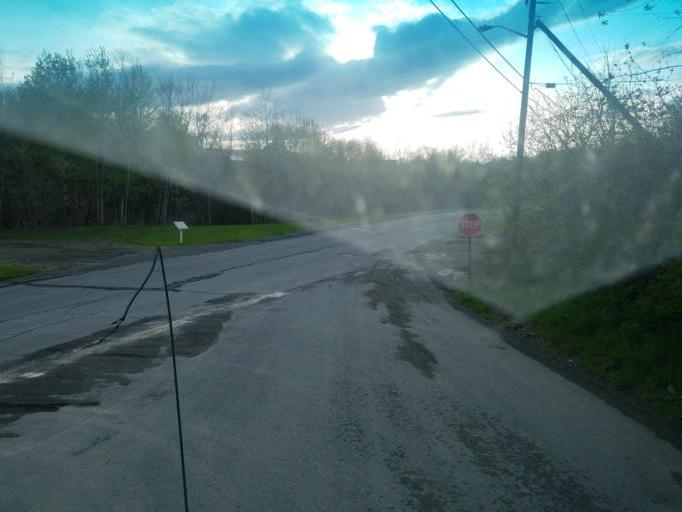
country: US
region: Maine
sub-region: Aroostook County
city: Caribou
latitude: 46.8586
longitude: -68.0083
